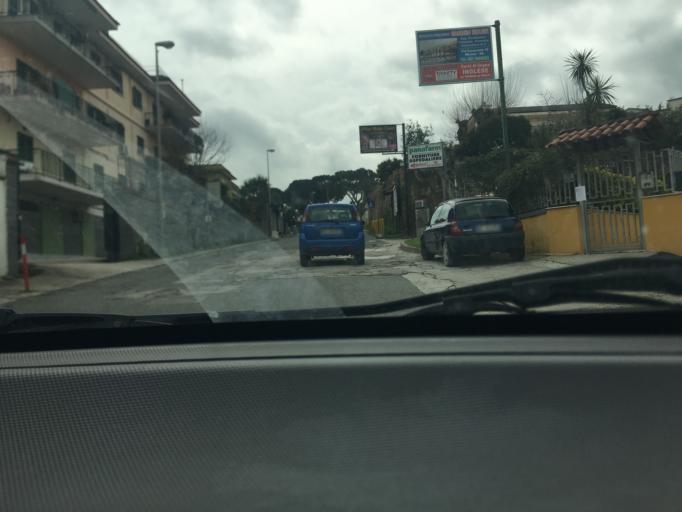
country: IT
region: Campania
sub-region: Provincia di Napoli
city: Marano di Napoli
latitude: 40.8918
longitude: 14.1801
